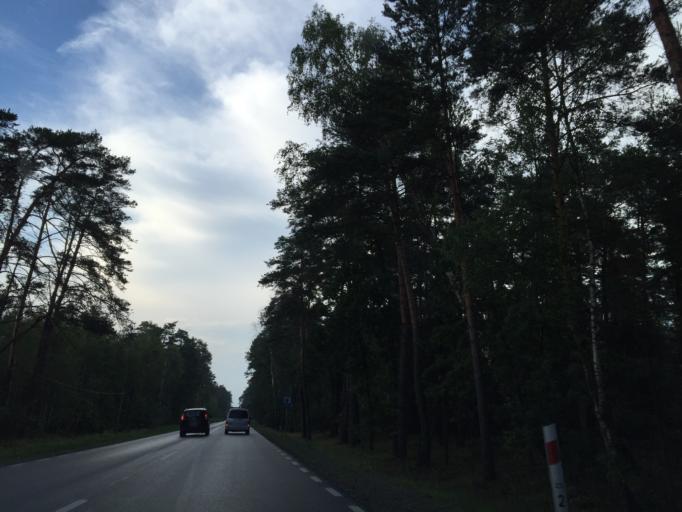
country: PL
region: Masovian Voivodeship
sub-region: Powiat wegrowski
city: Sadowne
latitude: 52.6167
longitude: 21.8405
